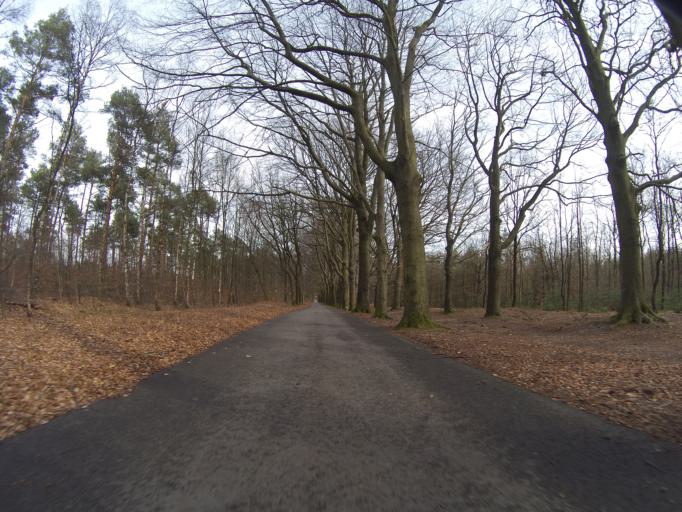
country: NL
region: Utrecht
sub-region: Gemeente Utrechtse Heuvelrug
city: Maarn
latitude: 52.0934
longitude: 5.3521
